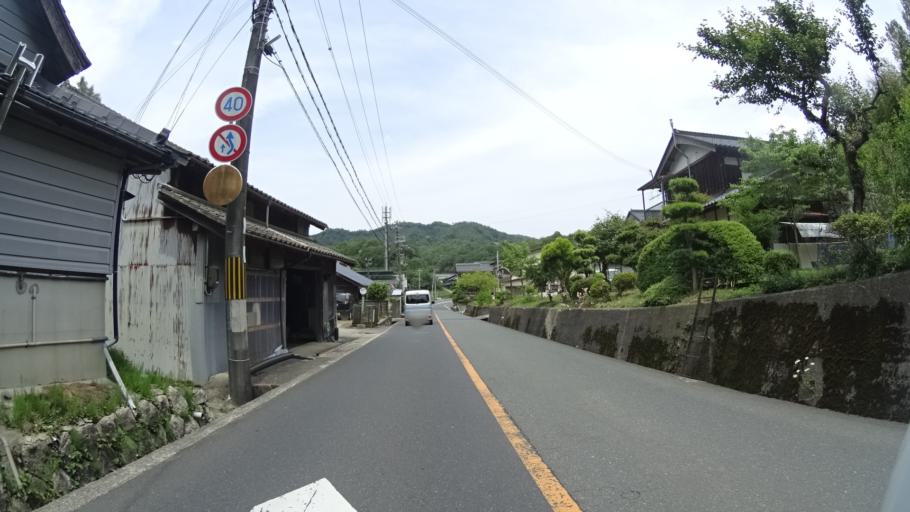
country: JP
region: Kyoto
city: Miyazu
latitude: 35.6834
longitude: 135.0571
